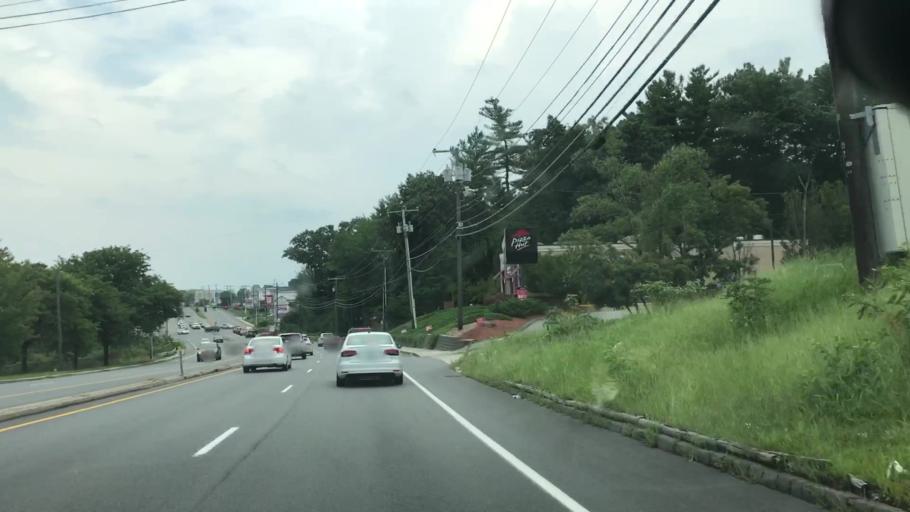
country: US
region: Massachusetts
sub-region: Middlesex County
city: Tyngsboro
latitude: 42.7167
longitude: -71.4428
